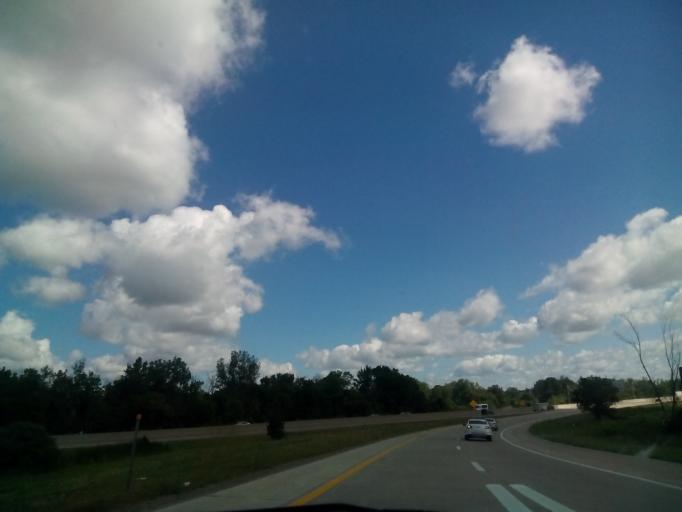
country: US
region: Michigan
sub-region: Genesee County
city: Flint
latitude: 42.9849
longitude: -83.7284
